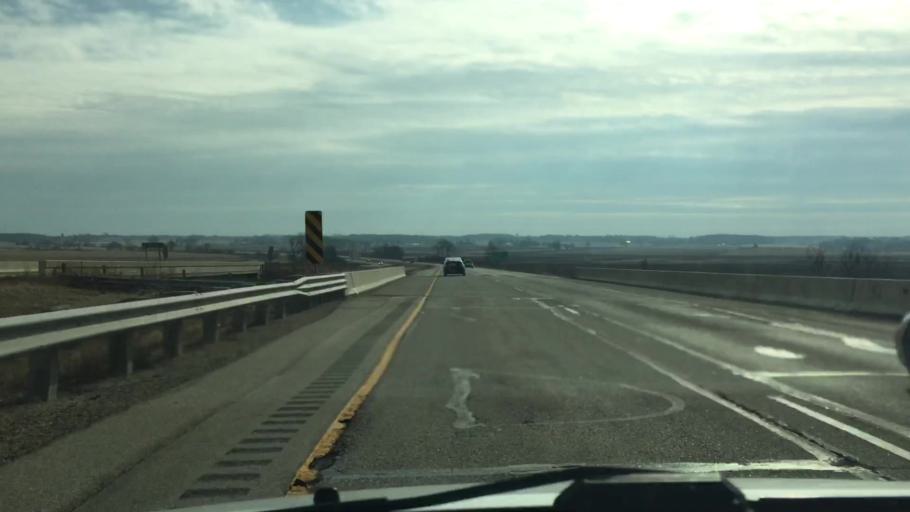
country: US
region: Wisconsin
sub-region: Walworth County
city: Elkhorn
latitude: 42.6528
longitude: -88.5074
